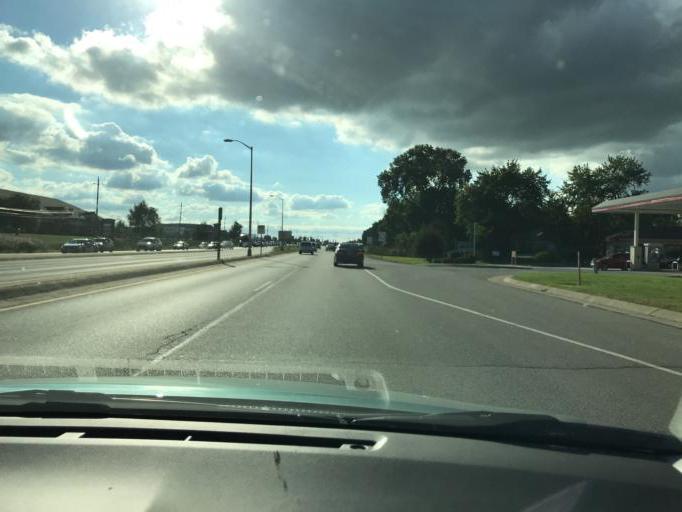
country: US
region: Wisconsin
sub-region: Kenosha County
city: Pleasant Prairie
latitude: 42.5669
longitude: -87.9143
